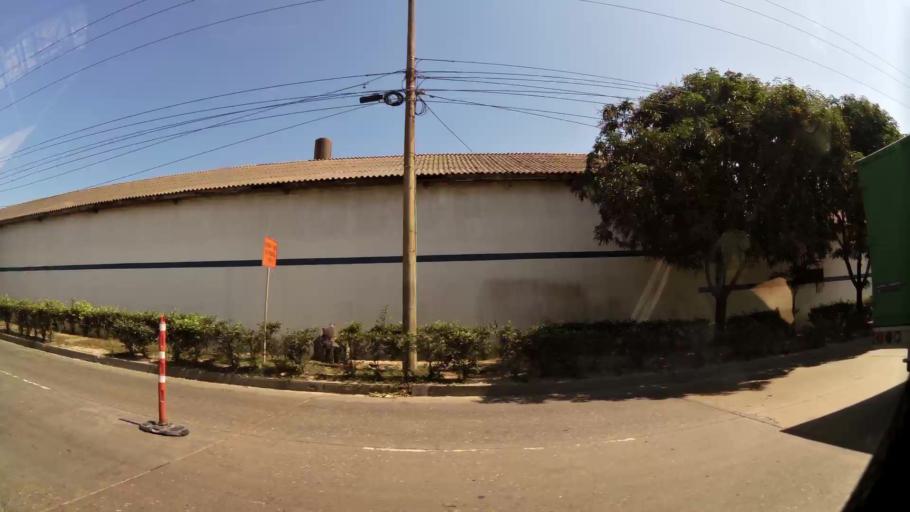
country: CO
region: Atlantico
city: Barranquilla
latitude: 11.0183
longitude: -74.7970
